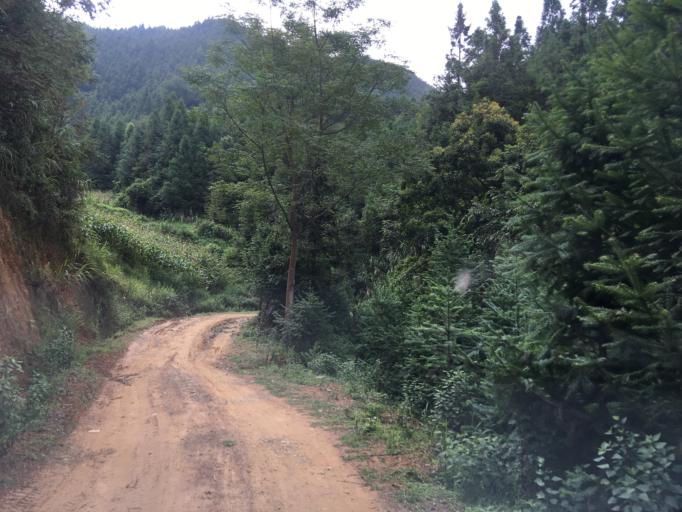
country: CN
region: Guangxi Zhuangzu Zizhiqu
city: Xinzhou
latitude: 24.8797
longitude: 105.8450
